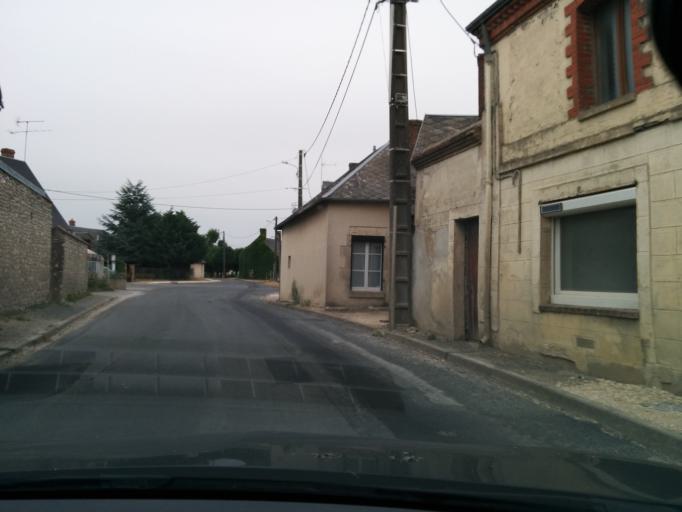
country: FR
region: Centre
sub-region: Departement du Loiret
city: Ascheres-le-Marche
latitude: 48.1372
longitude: 1.9685
